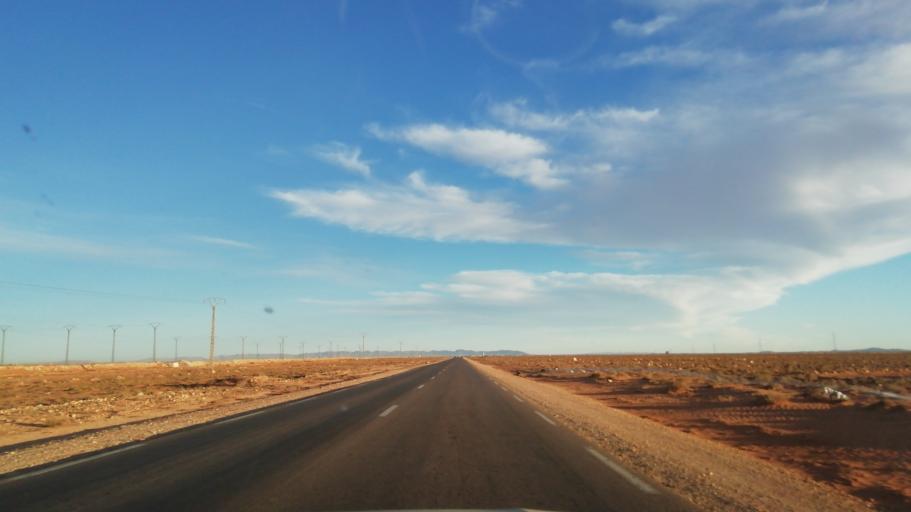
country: DZ
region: Wilaya de Naama
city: Naama
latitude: 33.7385
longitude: -0.7681
